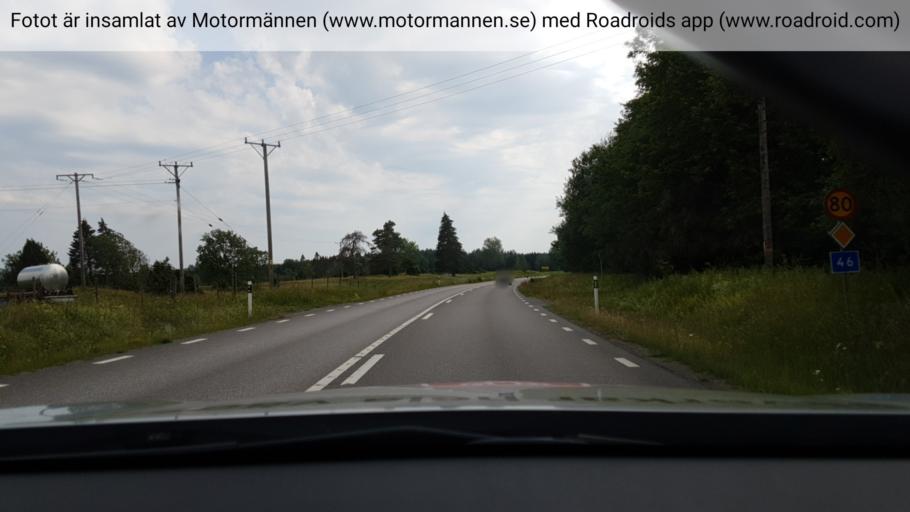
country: SE
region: Vaestra Goetaland
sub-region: Falkopings Kommun
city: Falkoeping
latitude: 58.0134
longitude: 13.5718
